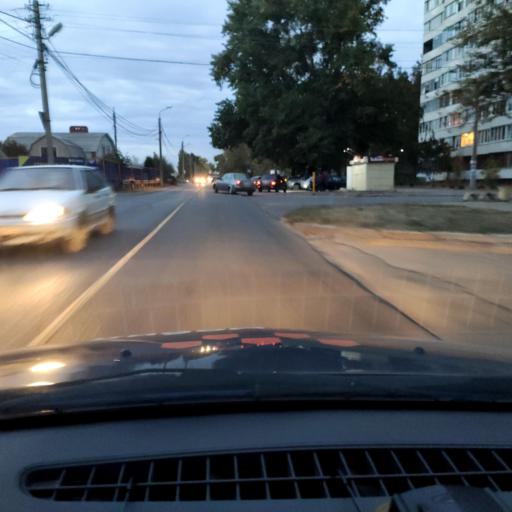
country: RU
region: Voronezj
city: Pridonskoy
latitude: 51.6871
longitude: 39.0794
